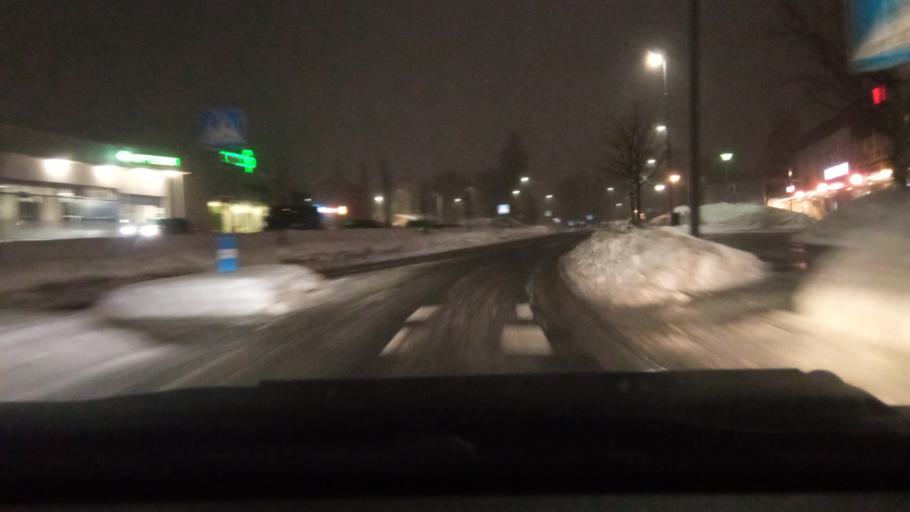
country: FI
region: Southern Ostrobothnia
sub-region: Jaerviseutu
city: Alajaervi
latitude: 63.0014
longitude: 23.8149
